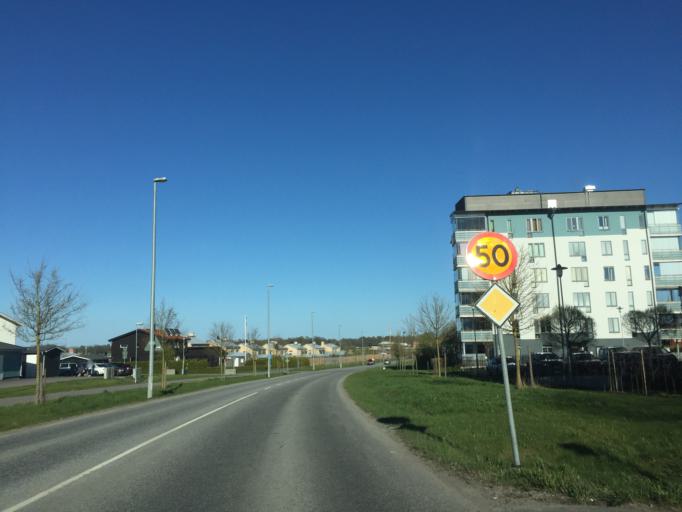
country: SE
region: OErebro
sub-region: Orebro Kommun
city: Orebro
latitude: 59.2660
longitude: 15.2544
